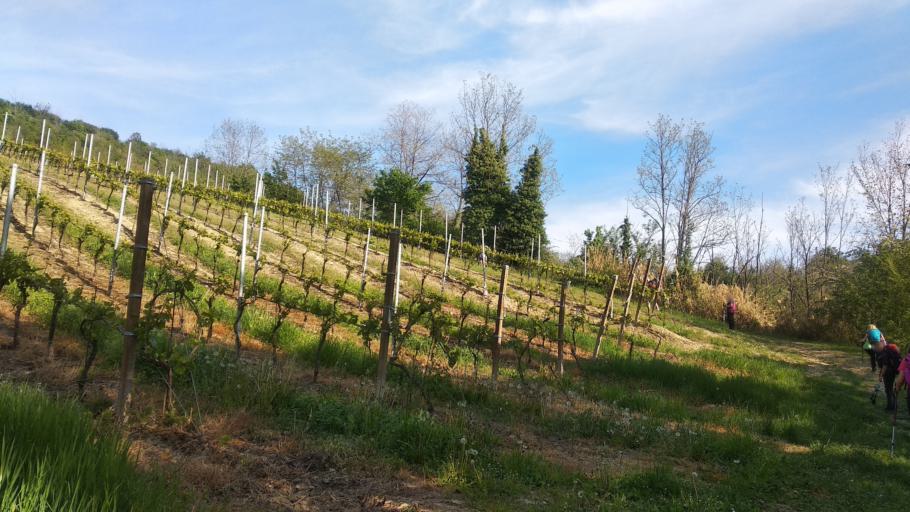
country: IT
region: Emilia-Romagna
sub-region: Provincia di Ravenna
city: Fognano
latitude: 44.2248
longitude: 11.7250
